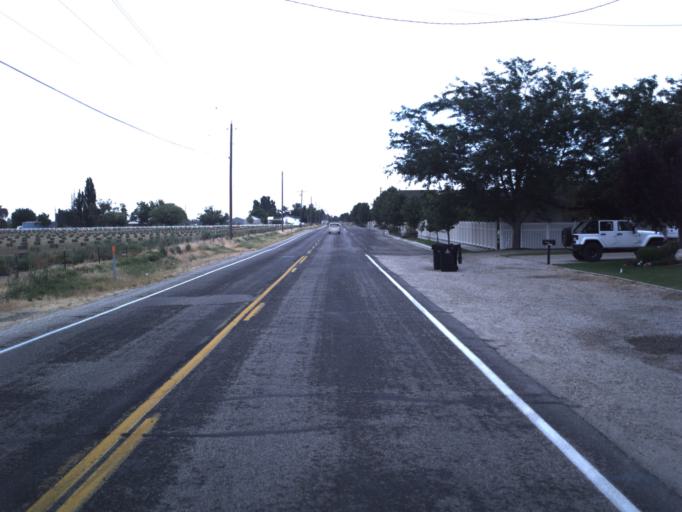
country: US
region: Utah
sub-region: Davis County
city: West Point
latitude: 41.0923
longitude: -112.1127
